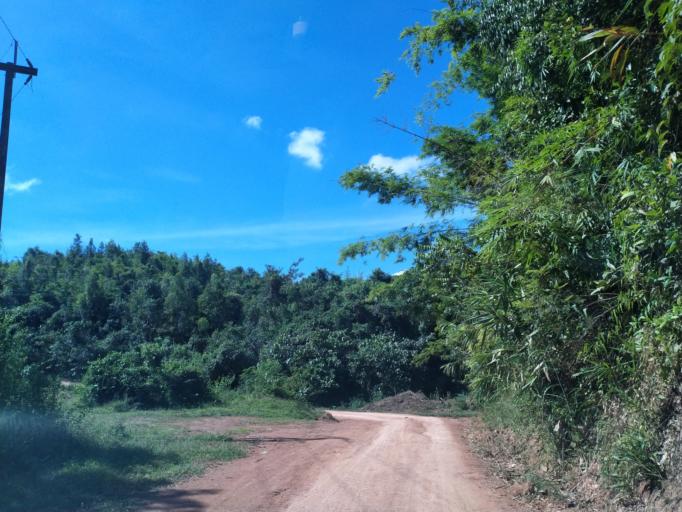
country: TH
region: Changwat Bueng Kan
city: Pak Khat
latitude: 18.6422
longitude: 103.0206
